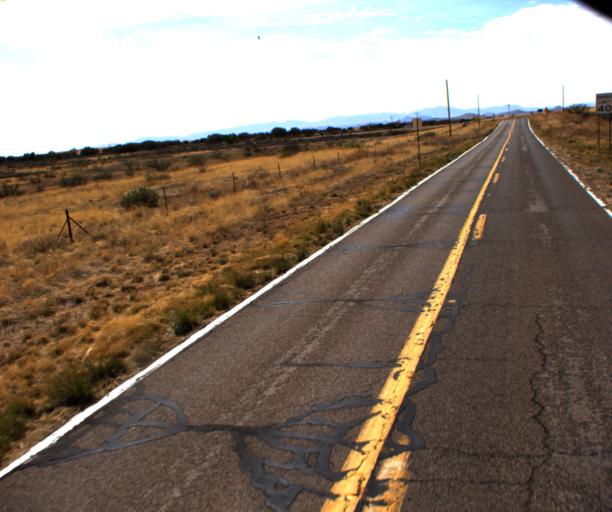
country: US
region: Arizona
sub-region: Cochise County
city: Willcox
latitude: 32.0068
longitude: -109.4361
